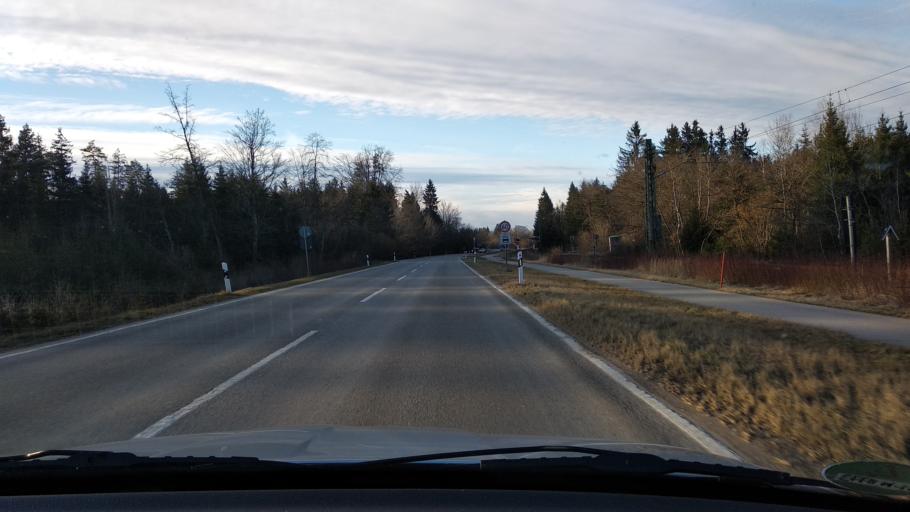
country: DE
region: Bavaria
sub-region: Upper Bavaria
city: Hohenkirchen-Siegertsbrunn
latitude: 48.0041
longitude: 11.7262
